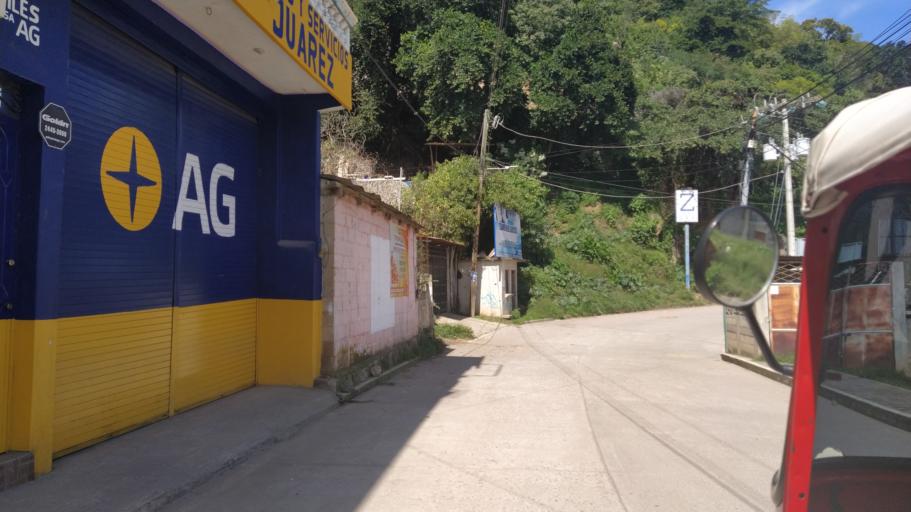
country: GT
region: Solola
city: San Pedro La Laguna
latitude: 14.6926
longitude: -91.2773
